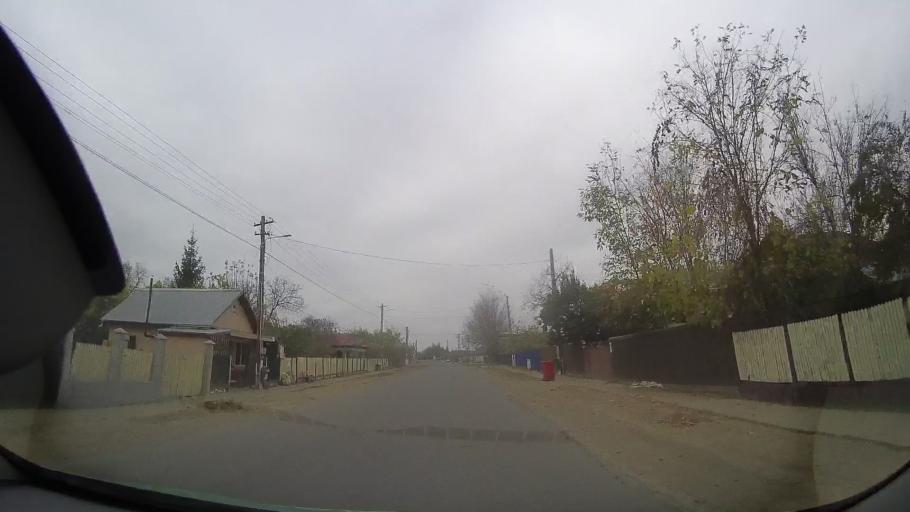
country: RO
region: Buzau
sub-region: Comuna Luciu
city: Luciu
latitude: 44.9728
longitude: 27.0751
